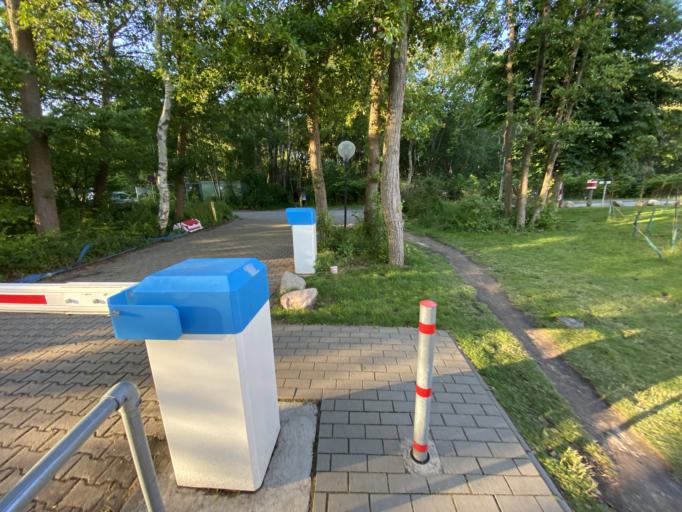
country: DE
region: Schleswig-Holstein
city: Sankt Peter-Ording
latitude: 54.3092
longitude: 8.6121
